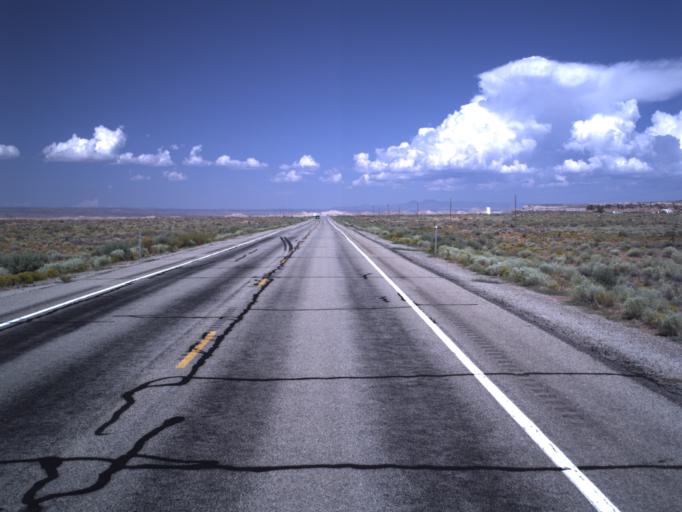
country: US
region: Utah
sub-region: San Juan County
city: Blanding
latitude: 37.1761
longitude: -109.5844
